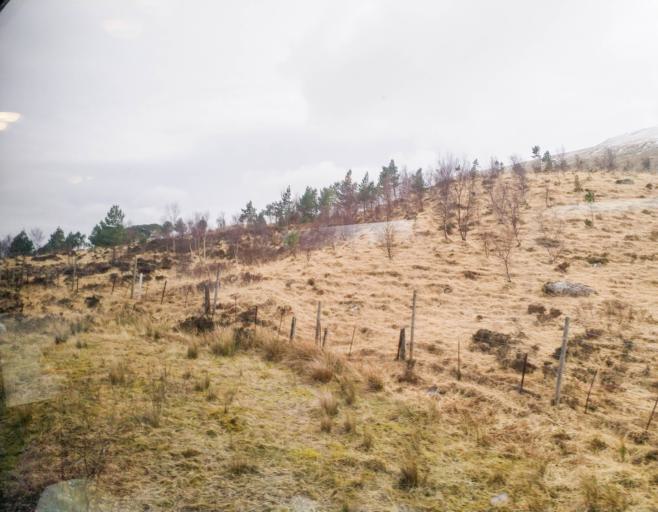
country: GB
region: Scotland
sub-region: Highland
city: Spean Bridge
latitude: 56.5689
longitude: -4.6955
